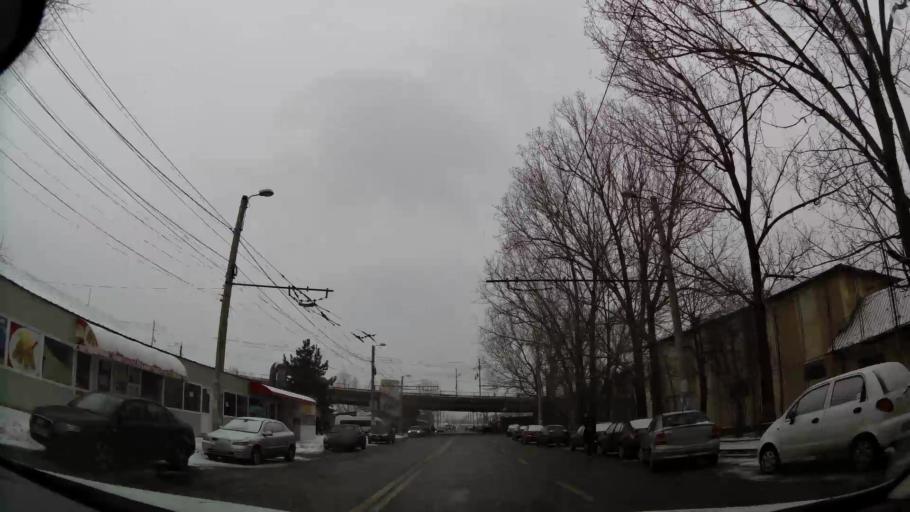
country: RO
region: Dambovita
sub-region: Municipiul Targoviste
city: Targoviste
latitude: 44.9173
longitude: 25.4532
